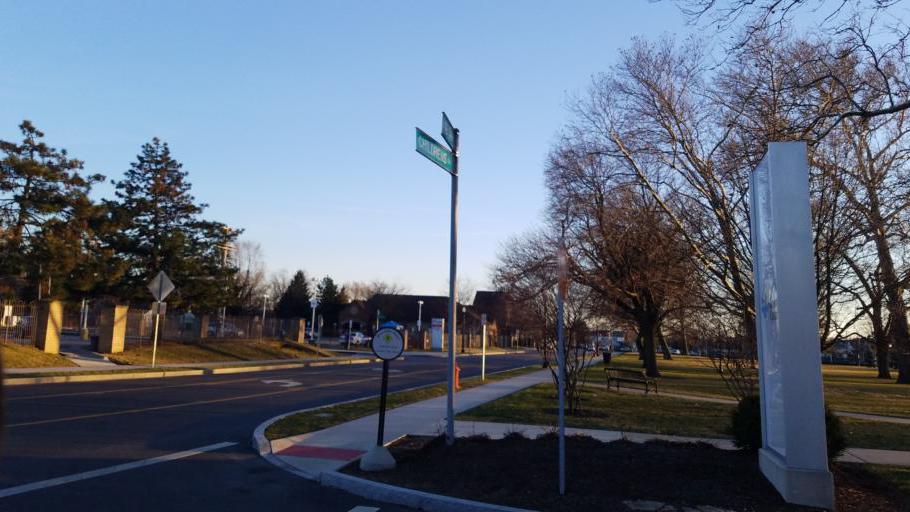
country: US
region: Ohio
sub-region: Franklin County
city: Columbus
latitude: 39.9523
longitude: -82.9766
